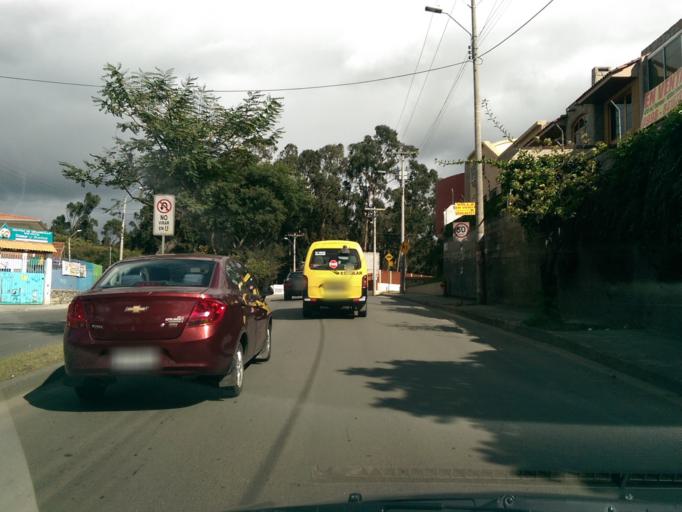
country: EC
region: Azuay
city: Cuenca
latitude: -2.9051
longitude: -79.0250
